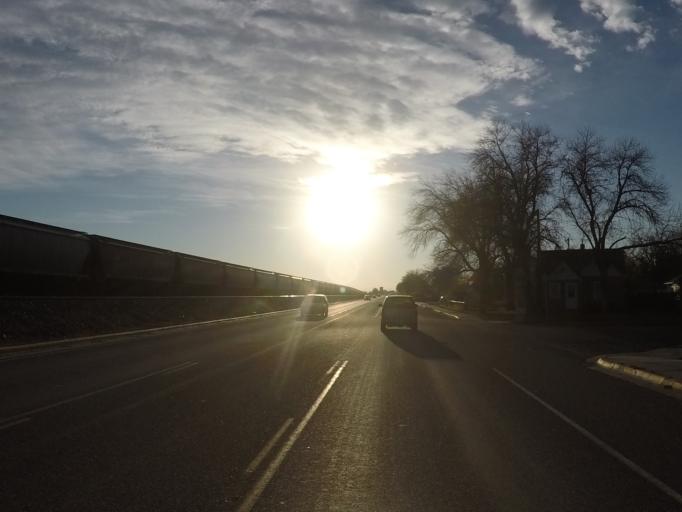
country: US
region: Montana
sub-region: Yellowstone County
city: Laurel
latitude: 45.6735
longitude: -108.7534
